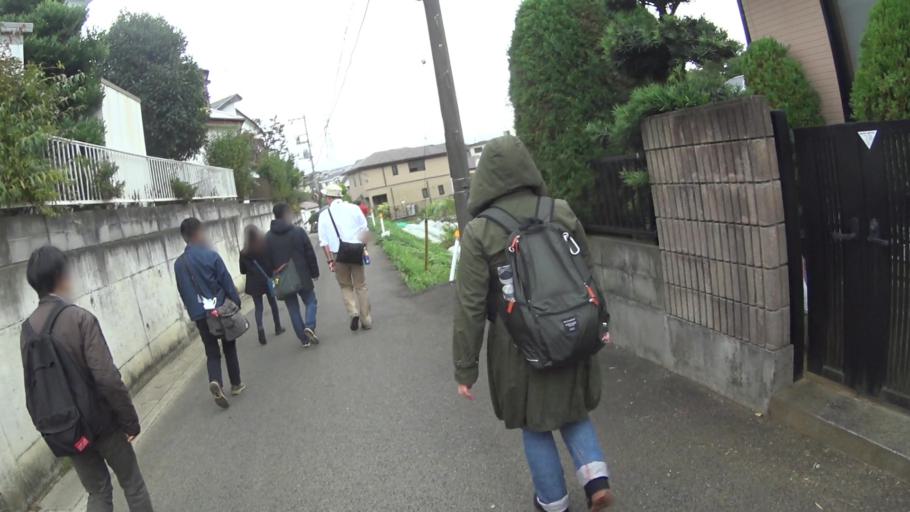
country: JP
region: Kanagawa
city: Hadano
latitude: 35.3905
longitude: 139.2208
